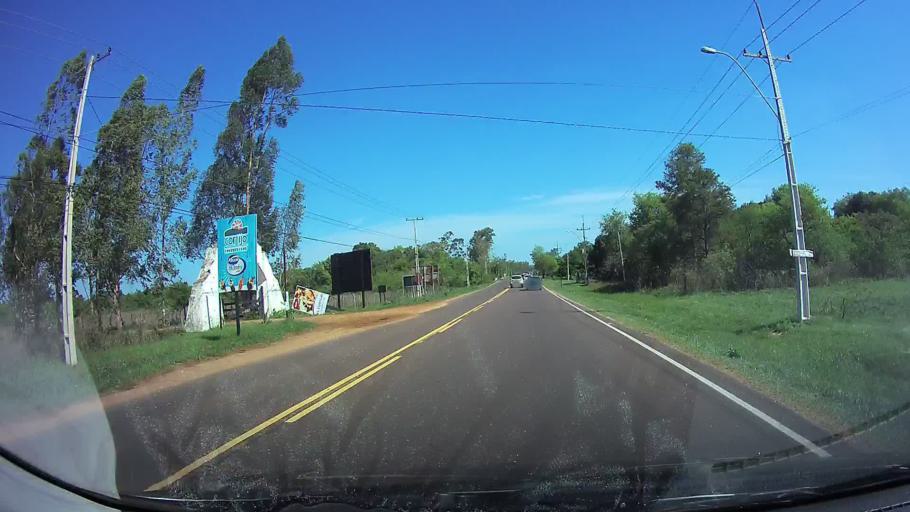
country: PY
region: Central
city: Ypacarai
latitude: -25.3654
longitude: -57.2643
